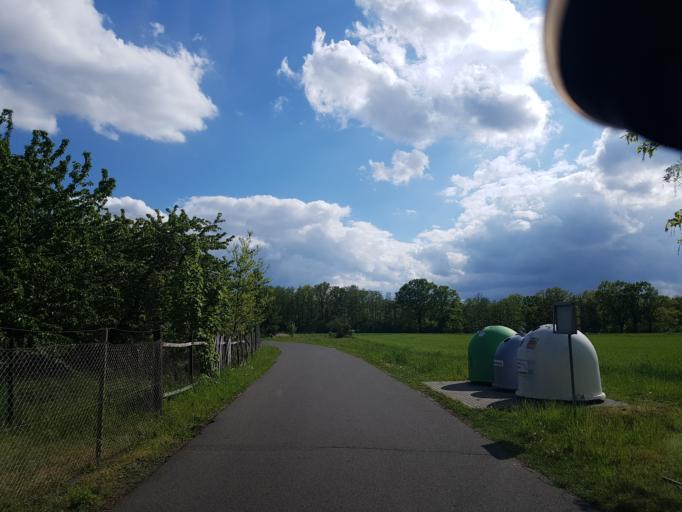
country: DE
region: Brandenburg
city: Drebkau
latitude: 51.6404
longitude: 14.2400
